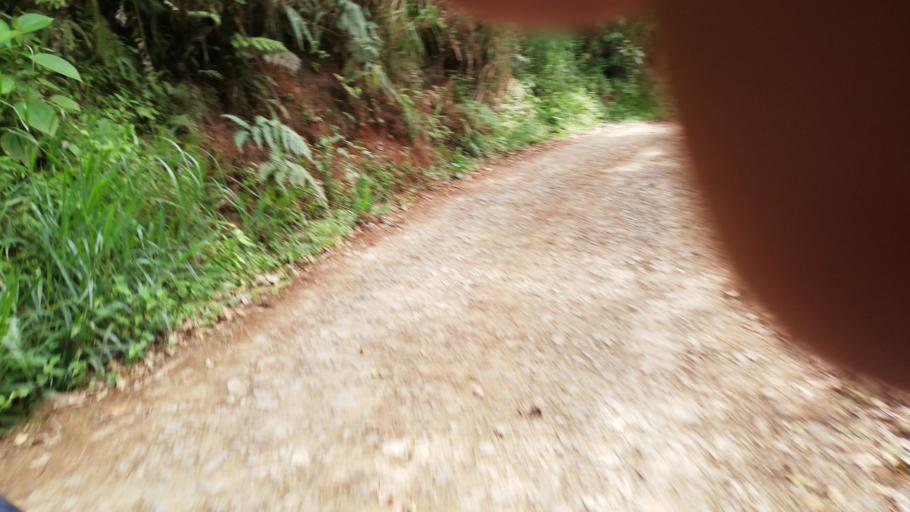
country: CO
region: Valle del Cauca
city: Yumbo
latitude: 3.6313
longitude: -76.5471
